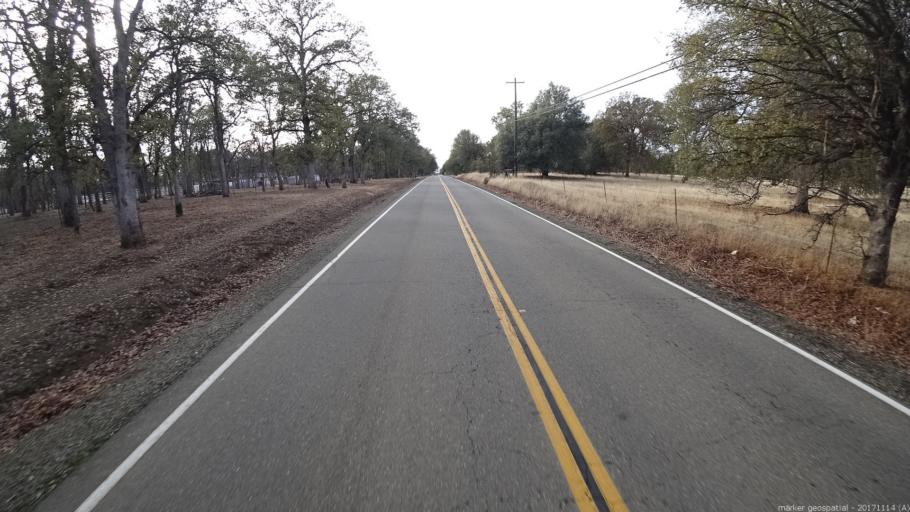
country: US
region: California
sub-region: Shasta County
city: Anderson
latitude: 40.3883
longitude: -122.4499
